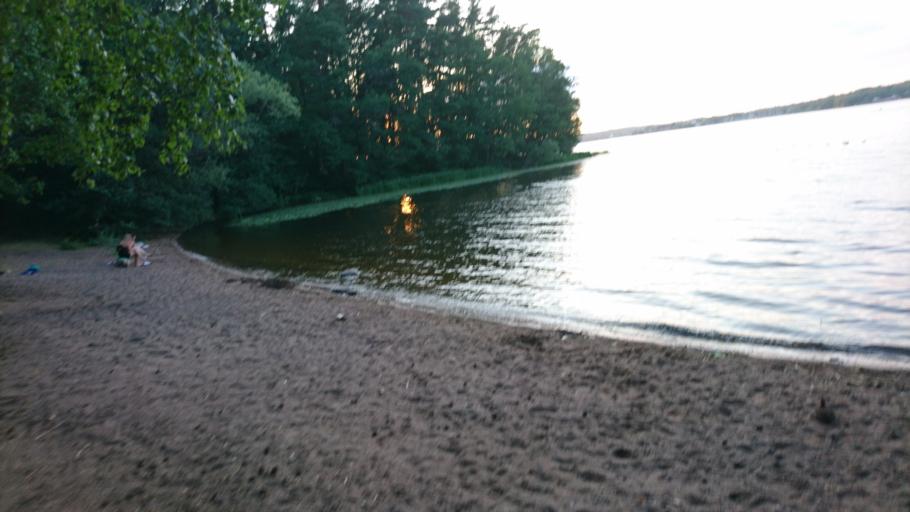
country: SE
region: Uppsala
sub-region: Uppsala Kommun
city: Saevja
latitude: 59.7716
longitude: 17.6393
